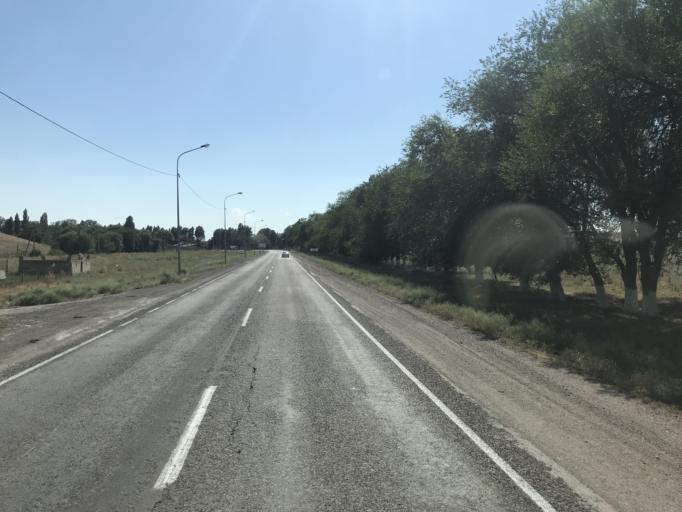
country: KZ
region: Zhambyl
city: Georgiyevka
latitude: 43.2382
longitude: 74.7652
